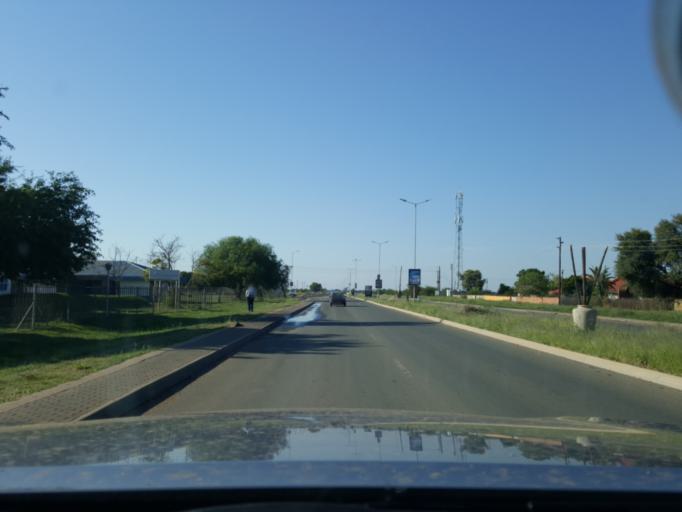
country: ZA
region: North-West
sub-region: Ngaka Modiri Molema District Municipality
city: Mmabatho
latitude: -25.8189
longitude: 25.6345
